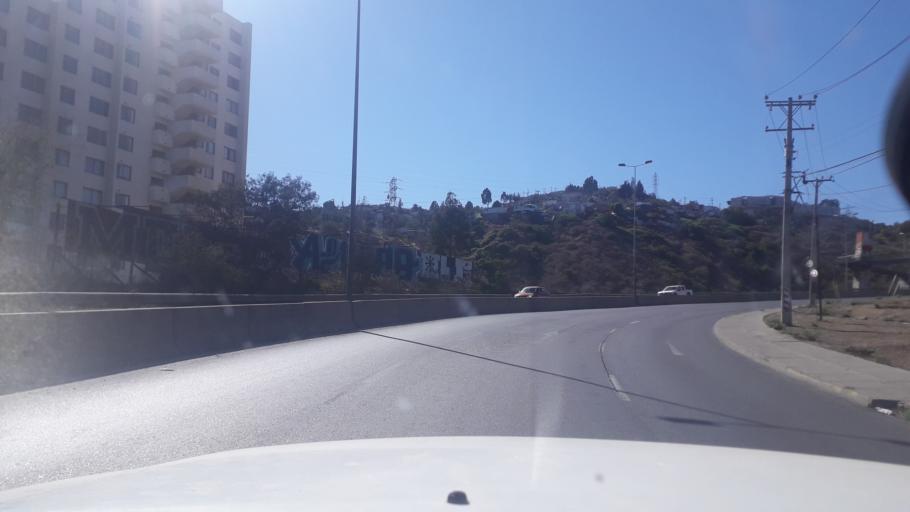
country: CL
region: Valparaiso
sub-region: Provincia de Valparaiso
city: Vina del Mar
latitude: -33.0354
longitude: -71.5163
